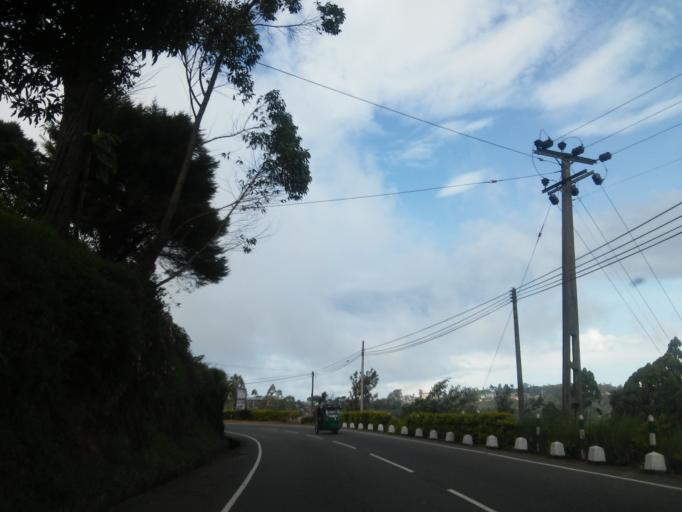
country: LK
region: Uva
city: Haputale
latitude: 6.7761
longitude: 80.9630
